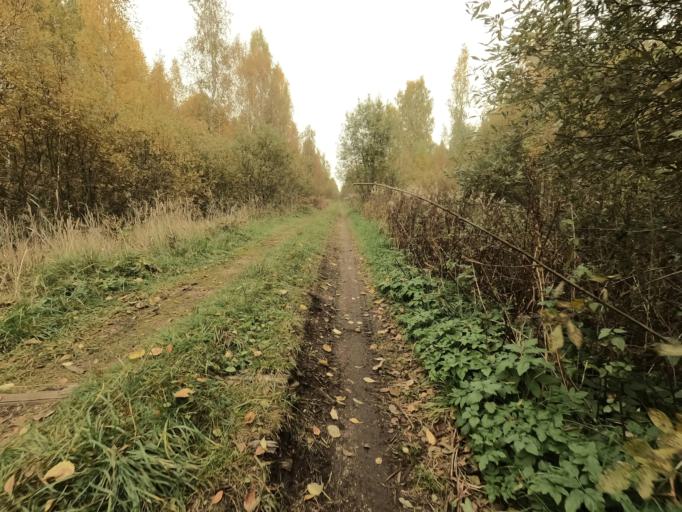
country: RU
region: Novgorod
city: Pankovka
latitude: 58.8892
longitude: 30.9488
